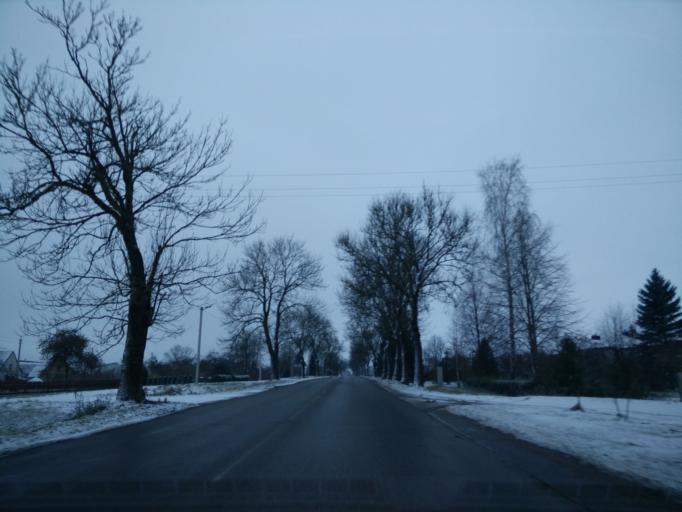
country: LT
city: Kelme
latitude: 55.6234
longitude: 22.9195
